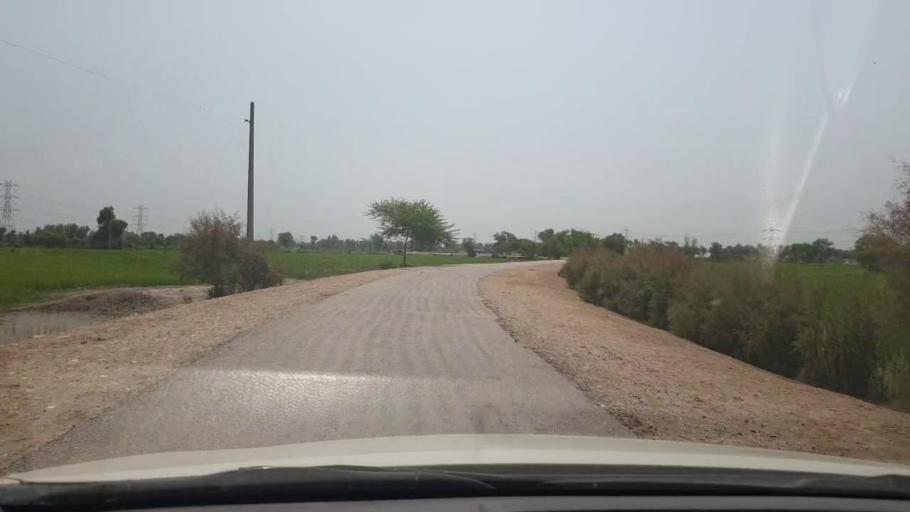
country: PK
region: Sindh
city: Shikarpur
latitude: 28.0197
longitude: 68.6598
